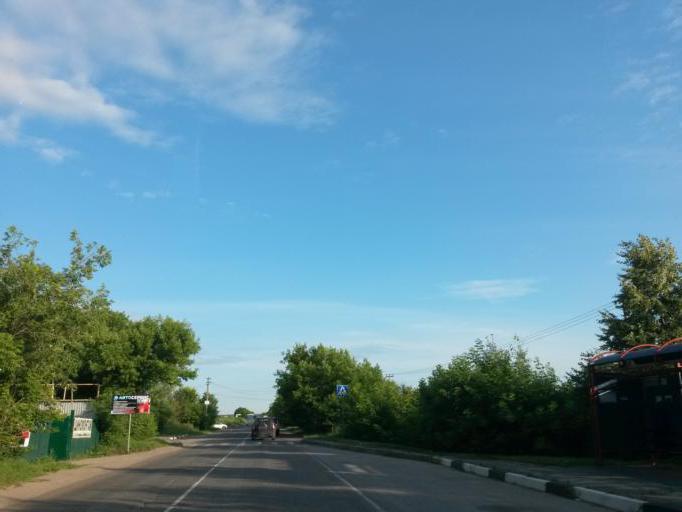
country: RU
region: Moskovskaya
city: Domodedovo
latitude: 55.4430
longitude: 37.6755
